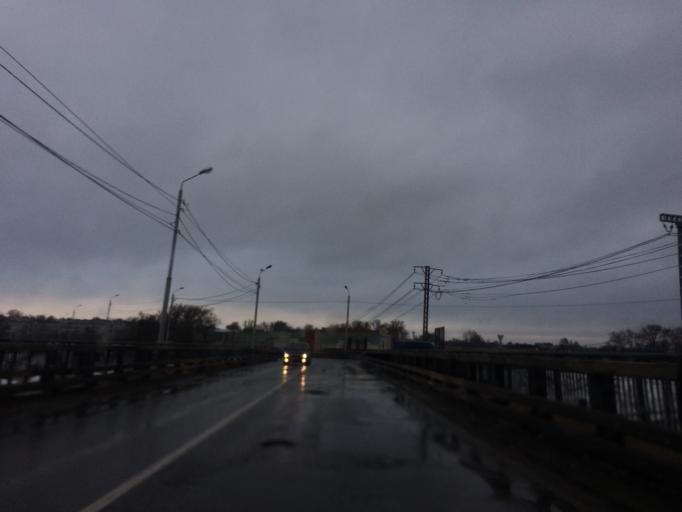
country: RU
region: Tula
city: Tula
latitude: 54.1907
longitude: 37.5707
